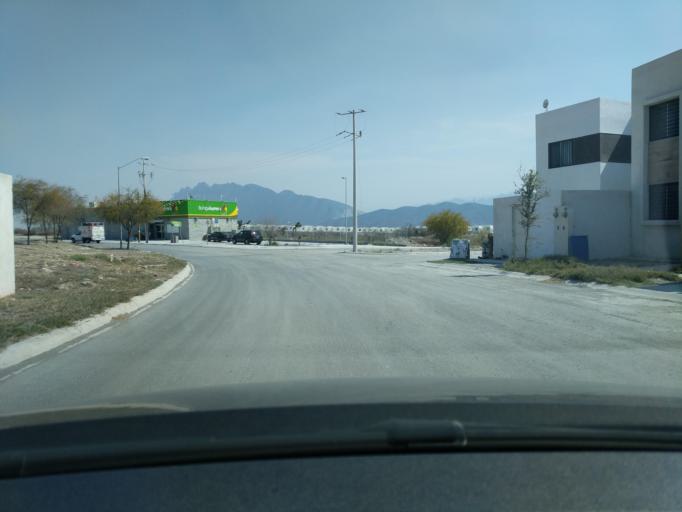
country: MX
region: Nuevo Leon
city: Garcia
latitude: 25.8151
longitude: -100.5413
